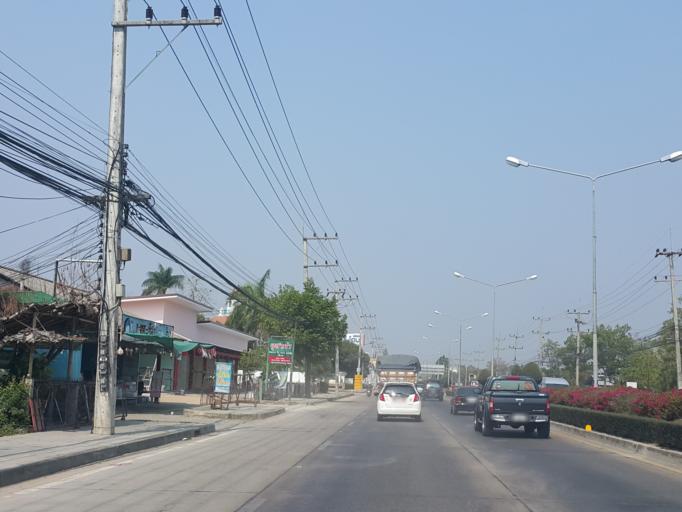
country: TH
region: Chiang Mai
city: Hang Dong
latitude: 18.7074
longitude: 98.9349
